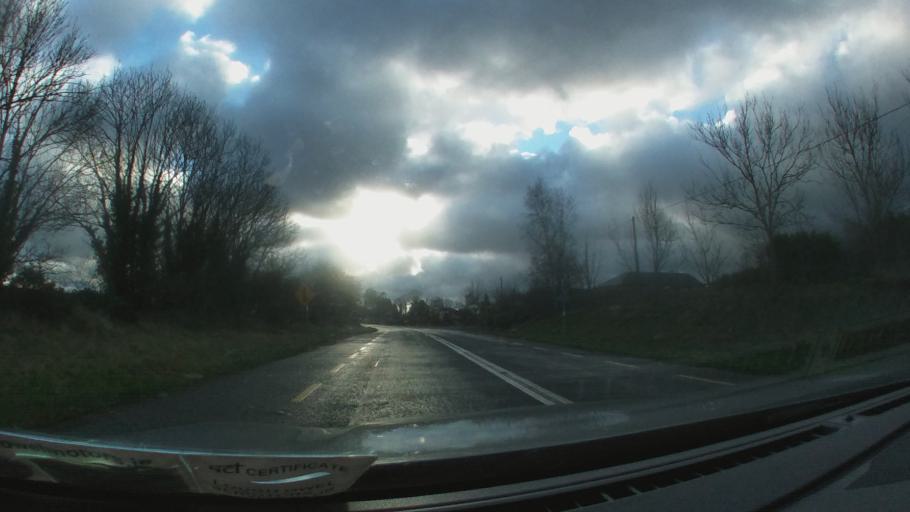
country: IE
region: Leinster
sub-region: Kilkenny
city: Thomastown
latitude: 52.5588
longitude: -7.1243
